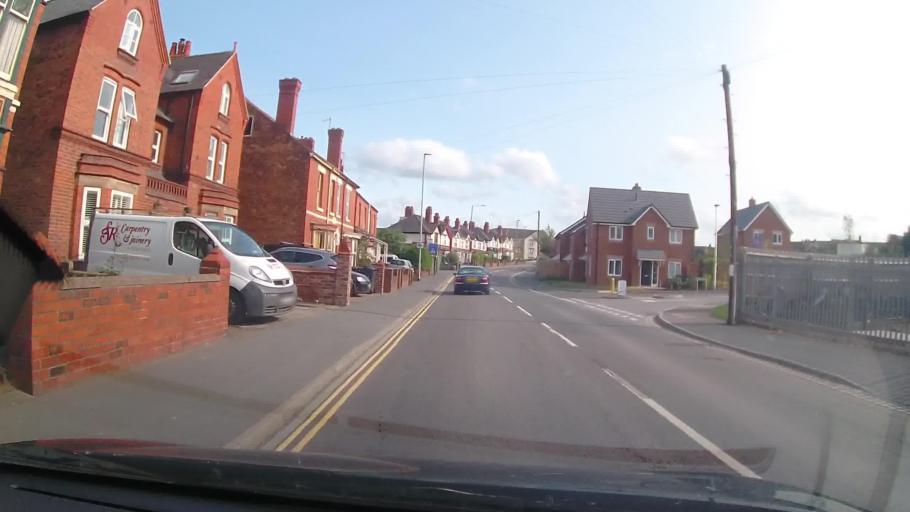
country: GB
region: England
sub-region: Shropshire
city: Shrewsbury
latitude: 52.7191
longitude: -2.7518
